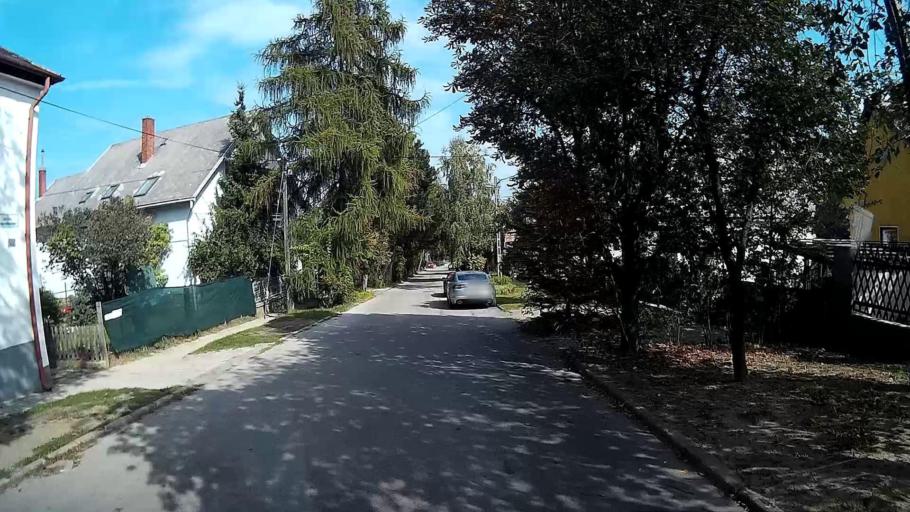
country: HU
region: Pest
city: Solymar
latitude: 47.5892
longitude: 18.9274
